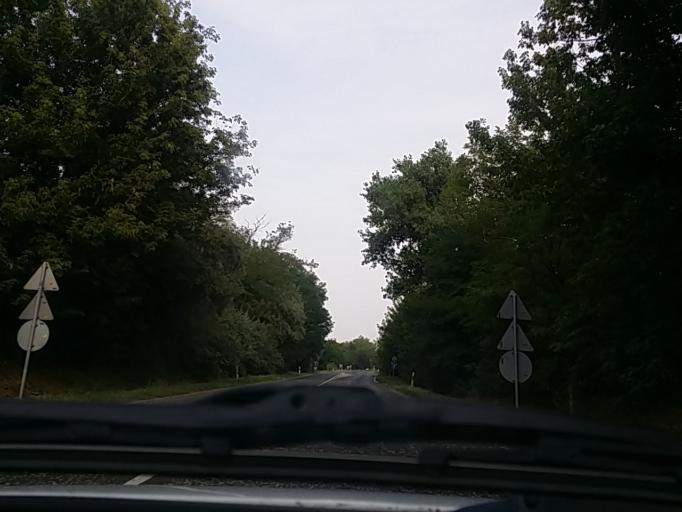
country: HU
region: Fejer
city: Etyek
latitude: 47.4947
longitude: 18.7481
